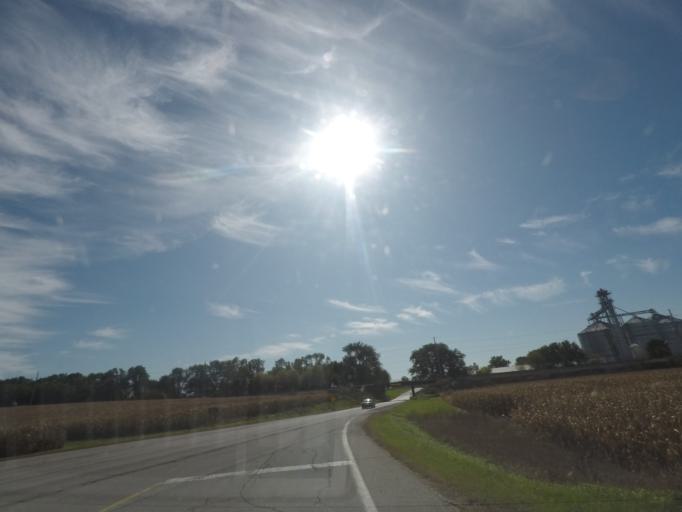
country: US
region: Iowa
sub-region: Story County
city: Nevada
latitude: 42.0202
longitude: -93.3096
